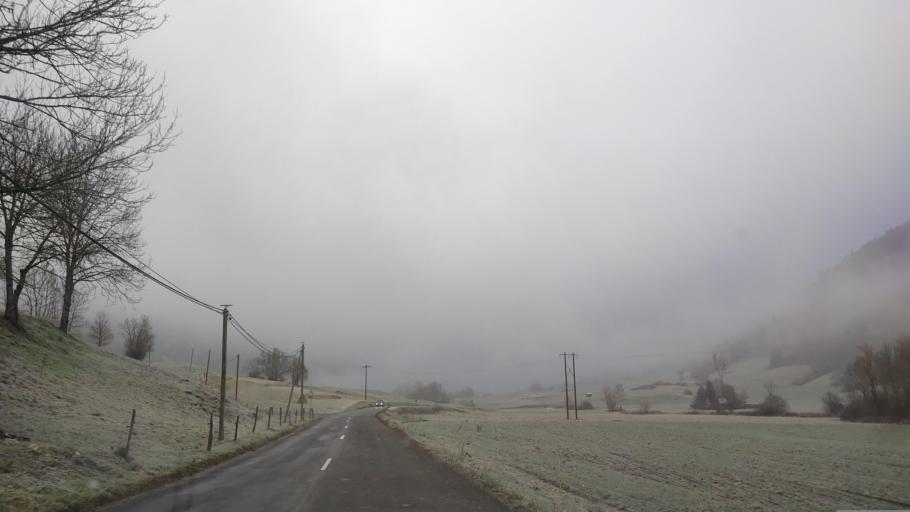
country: FR
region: Rhone-Alpes
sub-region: Departement de la Savoie
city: Coise-Saint-Jean-Pied-Gauthier
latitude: 45.6059
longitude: 6.1405
